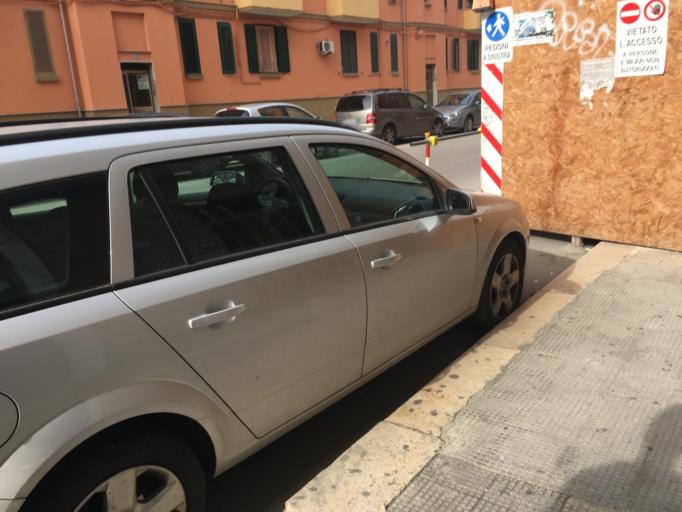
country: IT
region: Apulia
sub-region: Provincia di Bari
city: Bari
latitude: 41.1115
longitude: 16.8682
